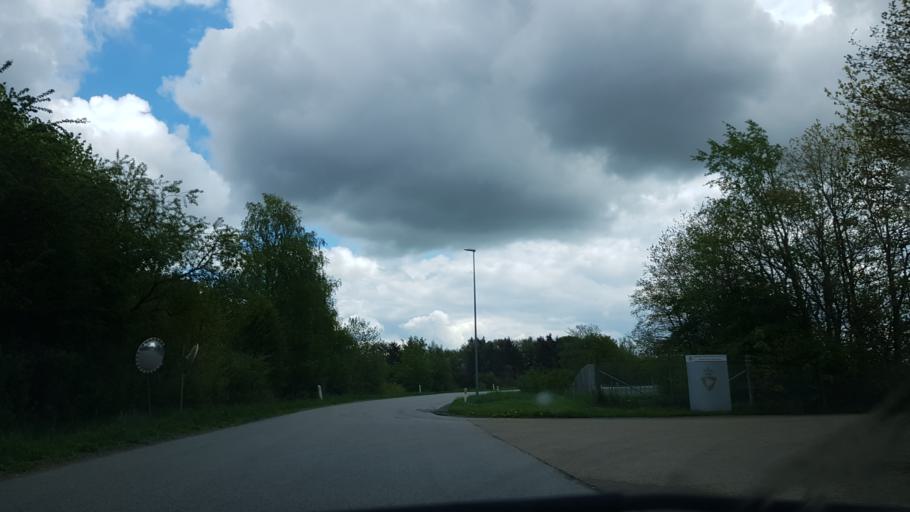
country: DK
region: South Denmark
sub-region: Haderslev Kommune
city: Vojens
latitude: 55.2353
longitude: 9.2690
